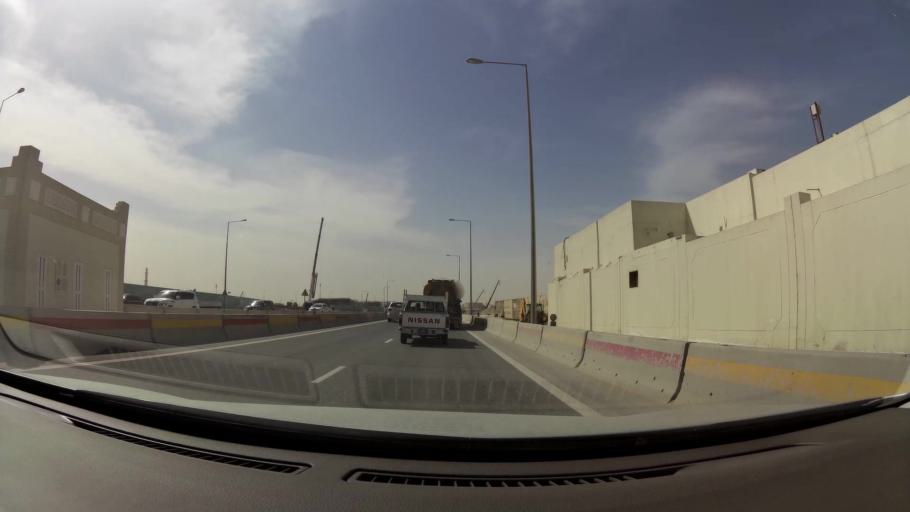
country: QA
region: Baladiyat ar Rayyan
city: Ar Rayyan
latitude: 25.3071
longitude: 51.4112
